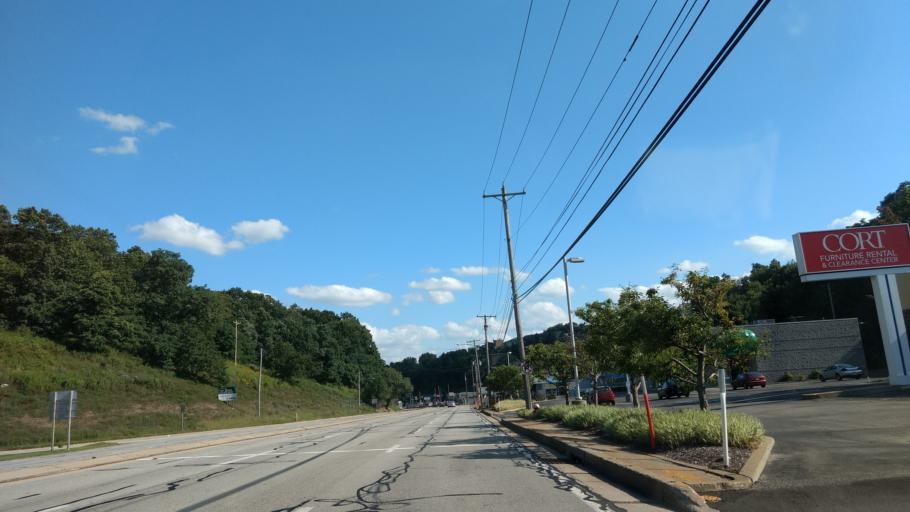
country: US
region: Pennsylvania
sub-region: Allegheny County
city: West View
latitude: 40.5495
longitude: -80.0190
